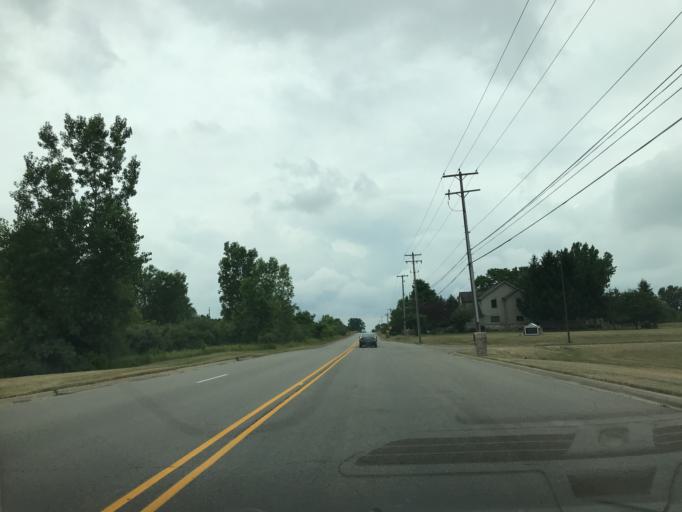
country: US
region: Michigan
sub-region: Eaton County
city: Waverly
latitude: 42.7231
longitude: -84.6621
